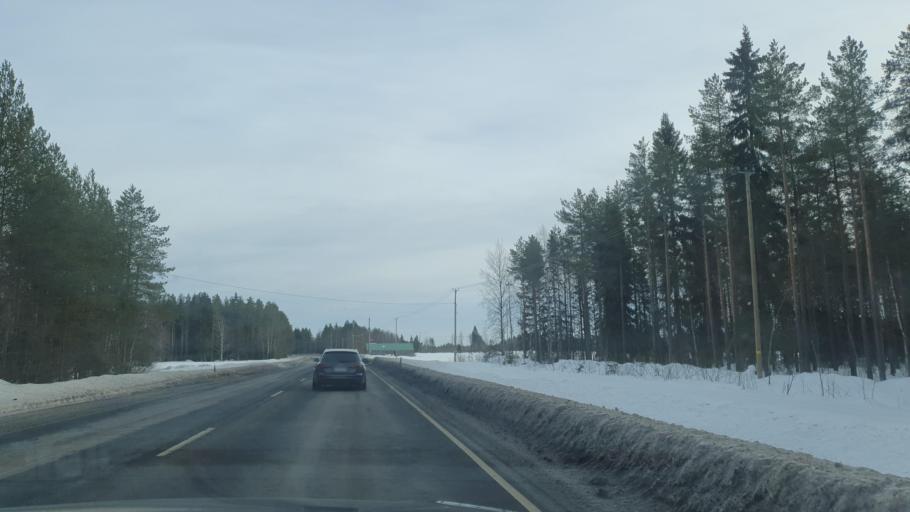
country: FI
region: Northern Ostrobothnia
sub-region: Oulunkaari
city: Utajaervi
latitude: 64.7820
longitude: 26.2649
